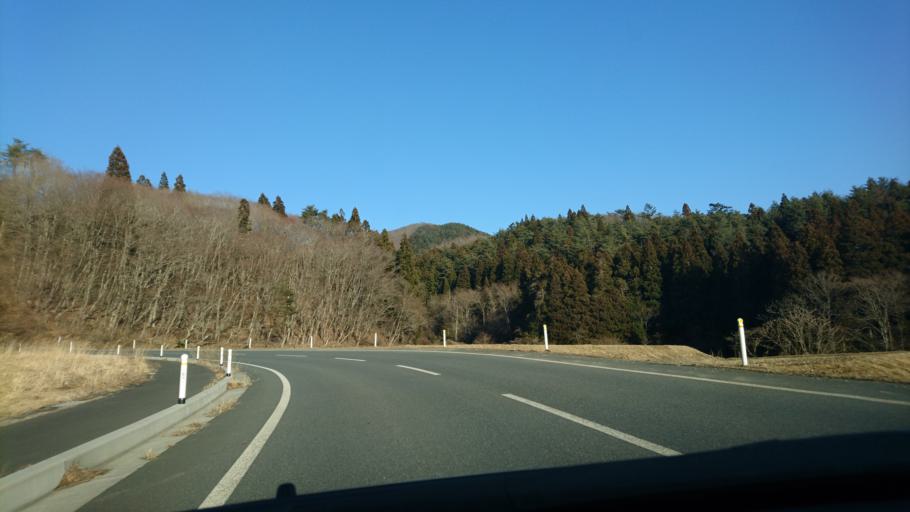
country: JP
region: Iwate
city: Ichinoseki
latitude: 38.8476
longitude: 141.3939
